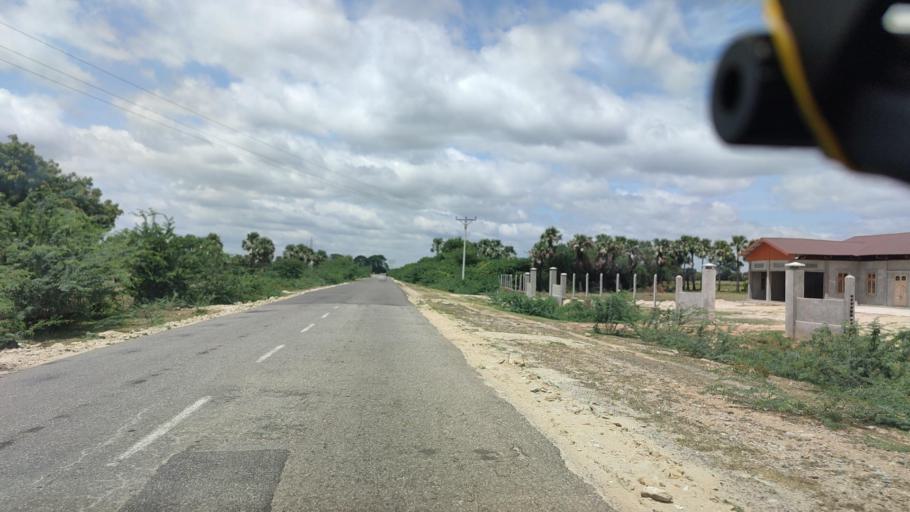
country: MM
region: Mandalay
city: Meiktila
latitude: 20.8383
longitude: 95.9396
